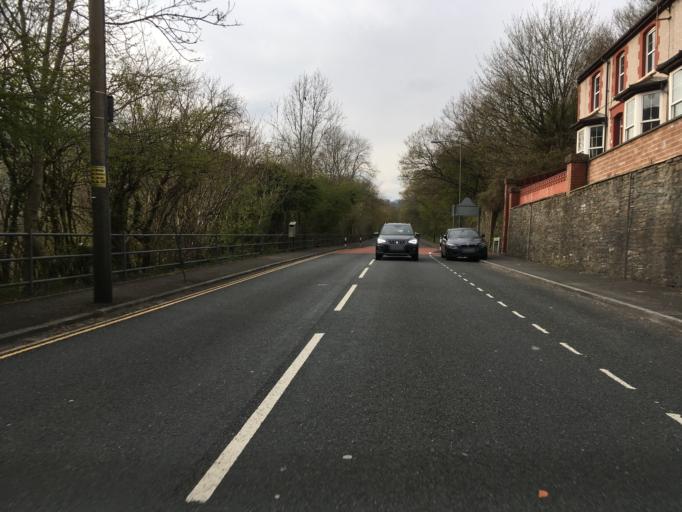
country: GB
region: Wales
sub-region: Caerphilly County Borough
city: Bedwas
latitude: 51.6207
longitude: -3.1809
